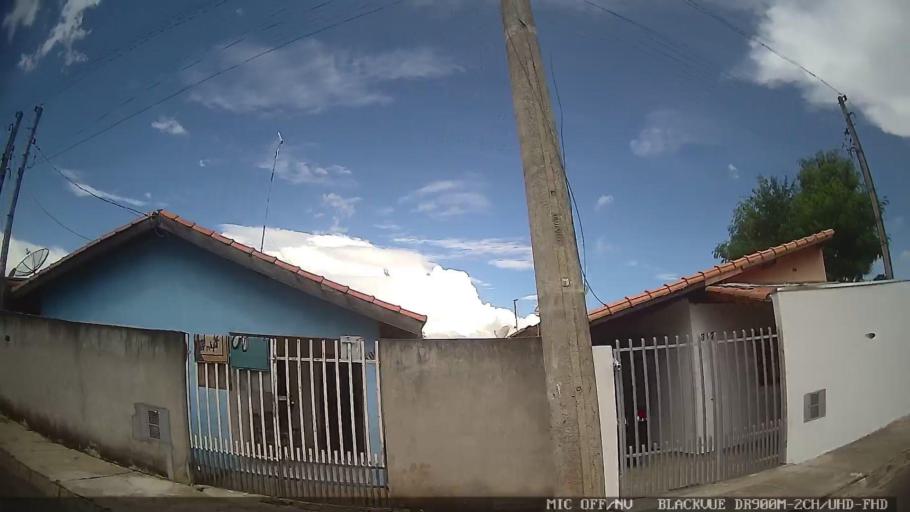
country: BR
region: Sao Paulo
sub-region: Conchas
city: Conchas
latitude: -23.0122
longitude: -48.0036
